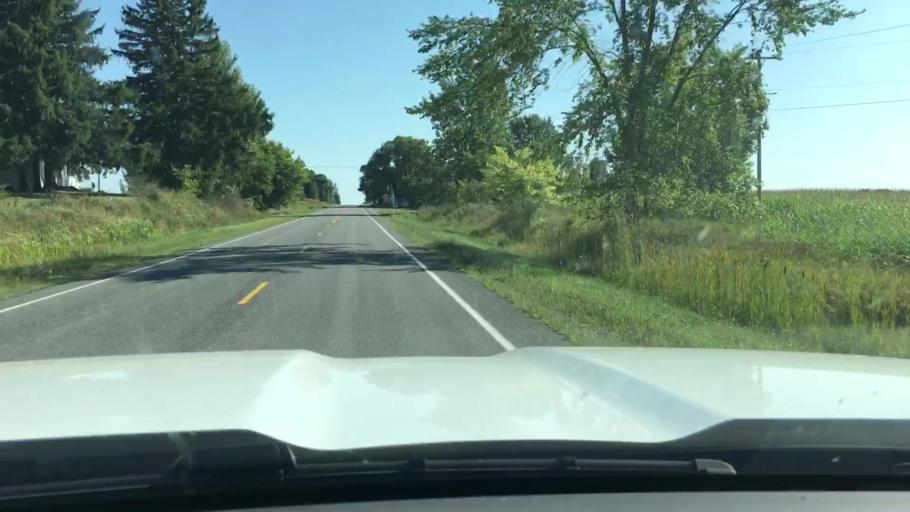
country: US
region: Michigan
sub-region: Muskegon County
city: Ravenna
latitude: 43.1668
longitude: -85.9280
